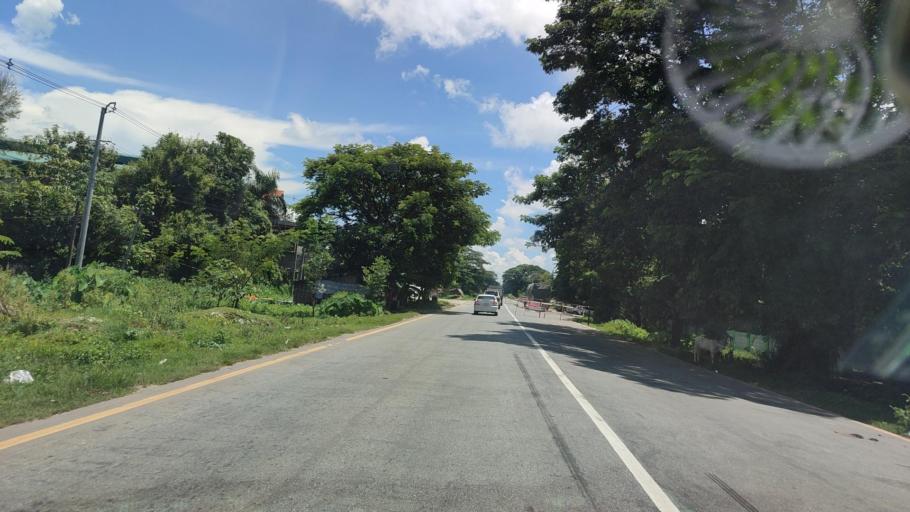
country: MM
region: Bago
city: Pyu
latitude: 18.2093
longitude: 96.5632
